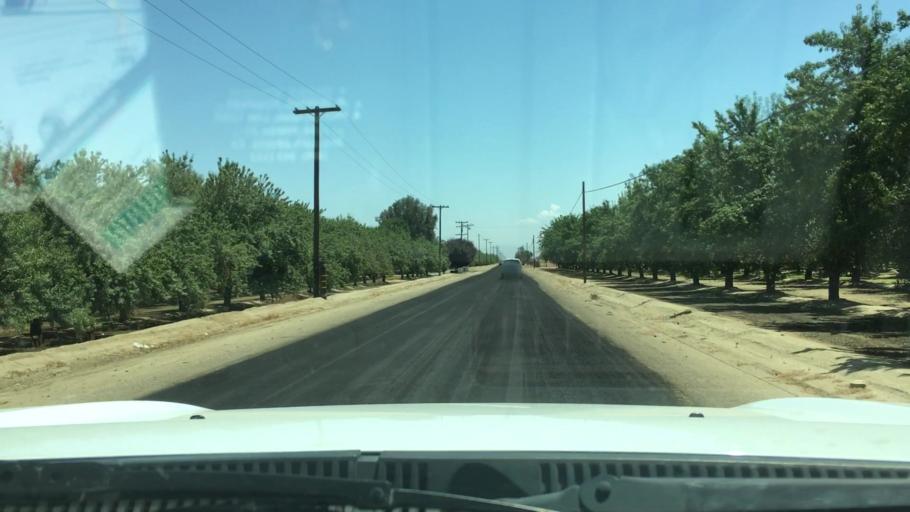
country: US
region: California
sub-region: Kern County
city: Shafter
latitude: 35.5291
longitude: -119.3201
